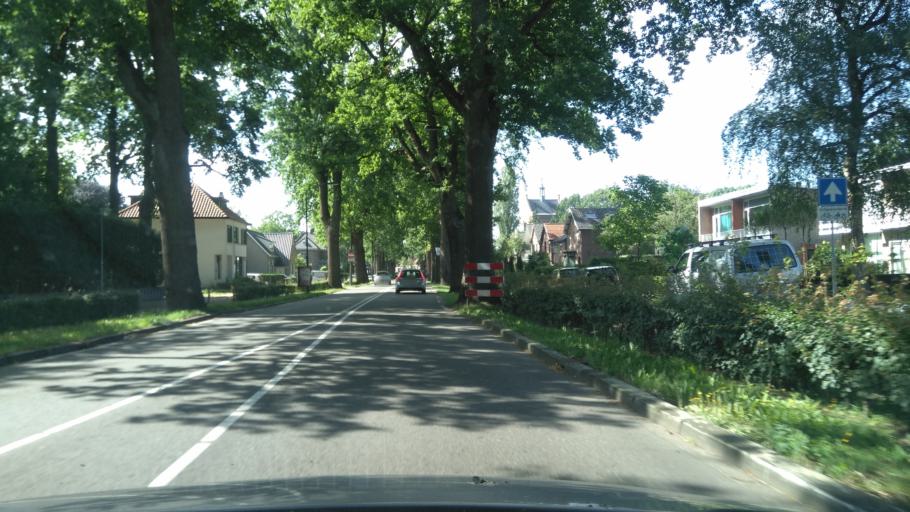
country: NL
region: North Brabant
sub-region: Gemeente Goirle
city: Goirle
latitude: 51.5284
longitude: 5.0633
